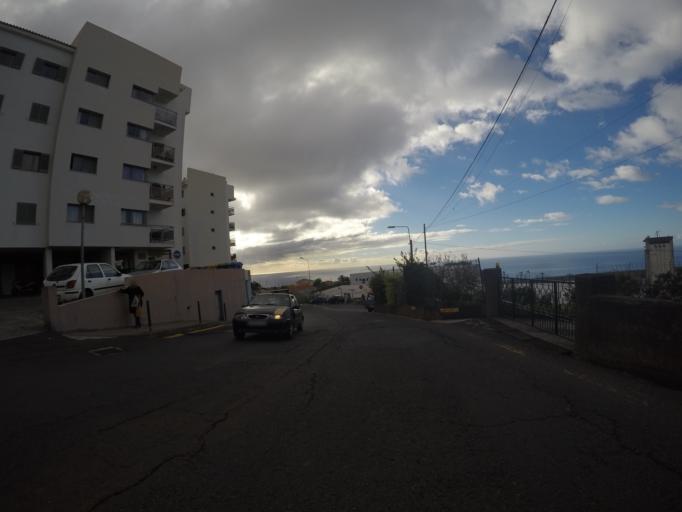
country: PT
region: Madeira
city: Canico
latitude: 32.6469
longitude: -16.8578
